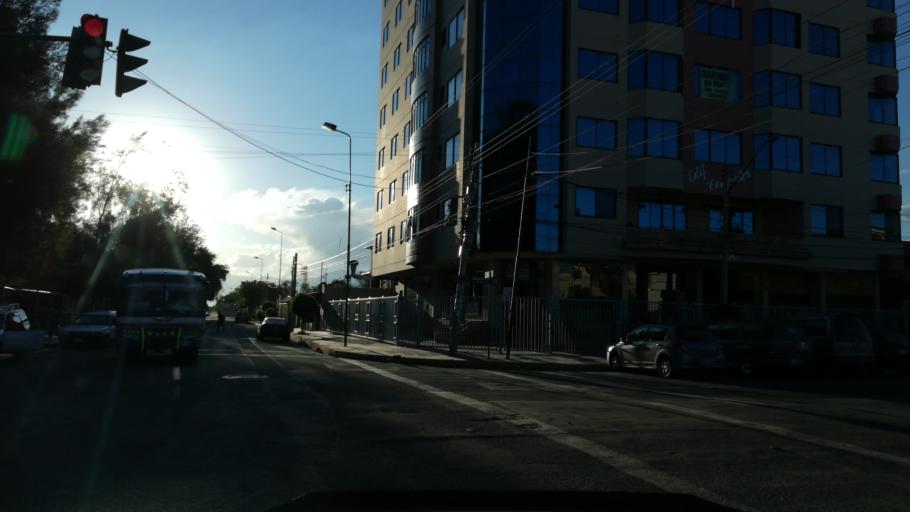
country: BO
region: Cochabamba
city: Cochabamba
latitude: -17.3985
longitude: -66.1741
